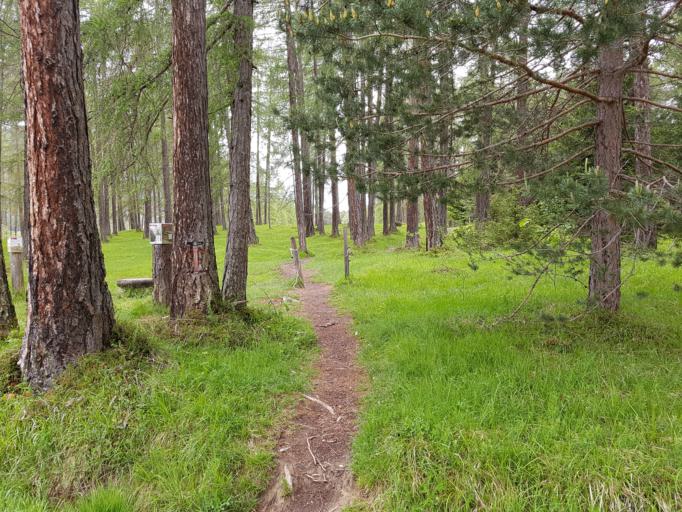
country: AT
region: Tyrol
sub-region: Politischer Bezirk Imst
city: Obsteig
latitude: 47.3017
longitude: 10.9334
